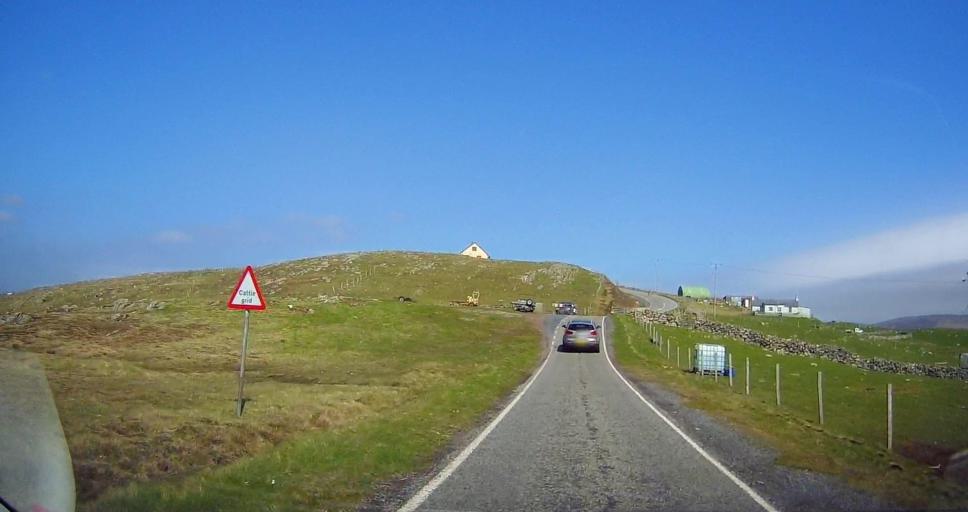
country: GB
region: Scotland
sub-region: Shetland Islands
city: Sandwick
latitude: 60.0937
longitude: -1.3234
